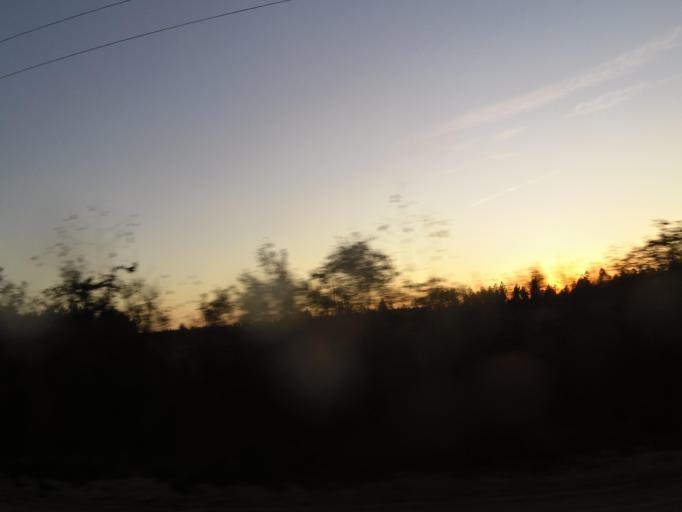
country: US
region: Florida
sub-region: Clay County
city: Asbury Lake
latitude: 29.9638
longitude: -81.7935
